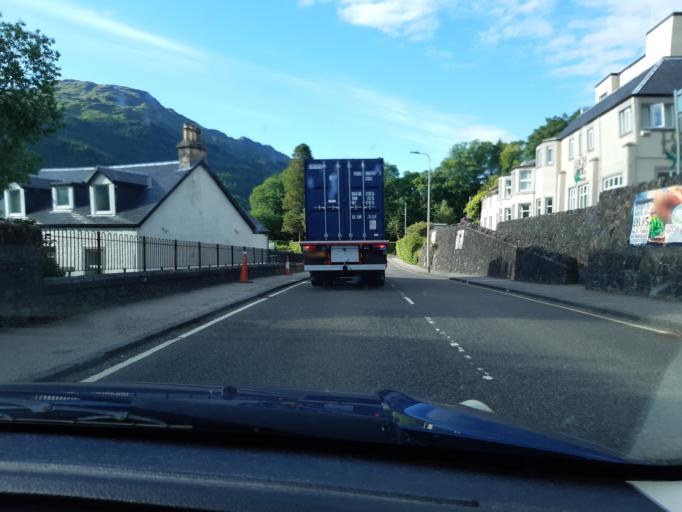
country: GB
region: Scotland
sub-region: Argyll and Bute
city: Garelochhead
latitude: 56.2040
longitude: -4.7436
